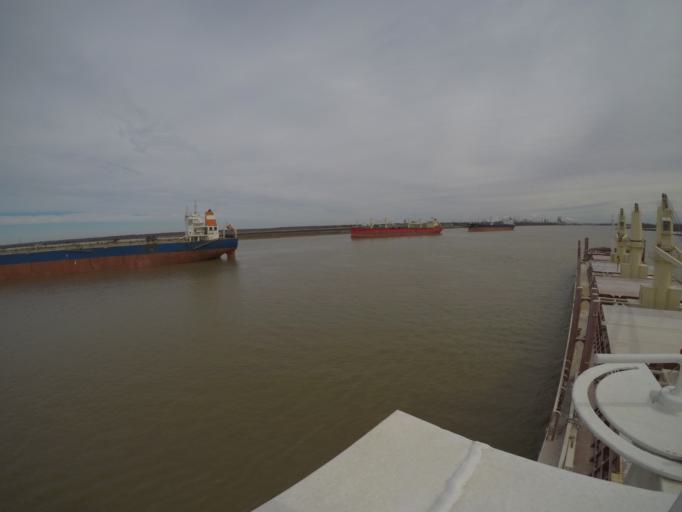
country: US
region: Louisiana
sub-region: Saint Charles Parish
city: Norco
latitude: 29.9947
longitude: -90.4416
